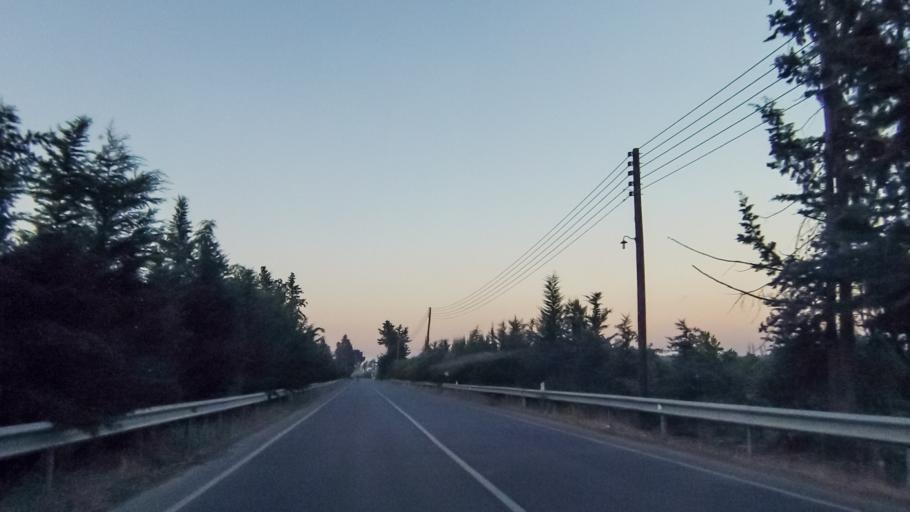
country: CY
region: Limassol
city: Ypsonas
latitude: 34.6518
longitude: 32.9865
